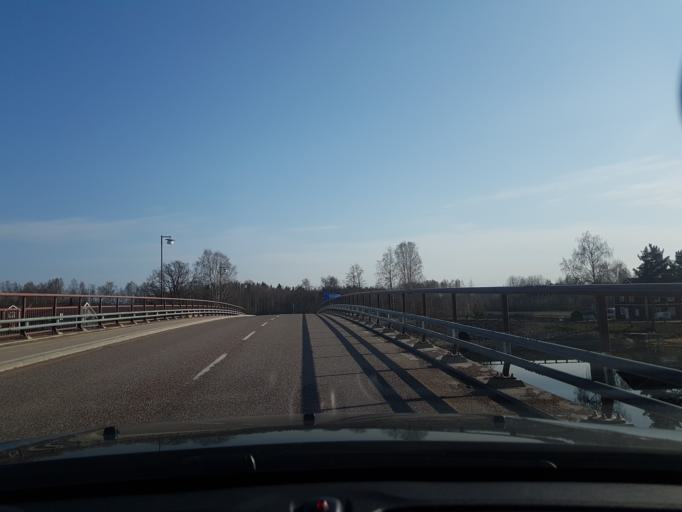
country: SE
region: Dalarna
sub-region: Borlange Kommun
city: Ornas
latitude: 60.4628
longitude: 15.5645
